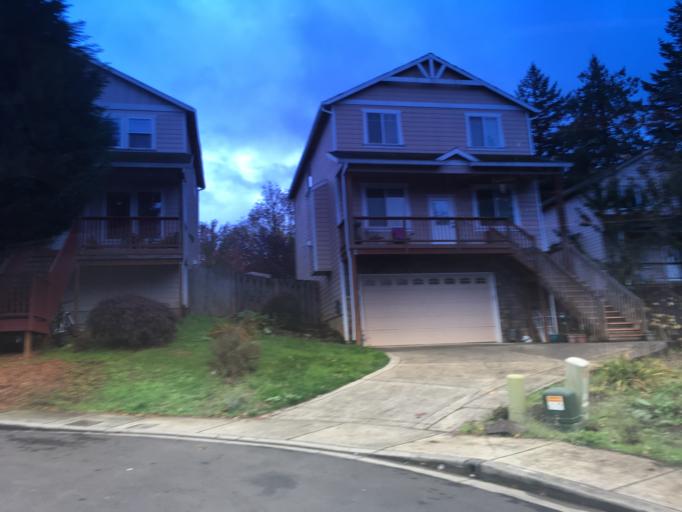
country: US
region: Oregon
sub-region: Multnomah County
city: Fairview
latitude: 45.5231
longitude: -122.4386
